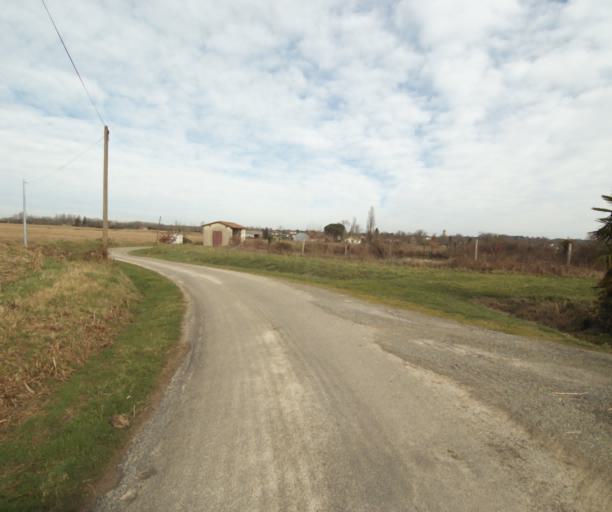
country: FR
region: Aquitaine
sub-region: Departement des Landes
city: Gabarret
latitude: 43.9795
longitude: 0.0017
